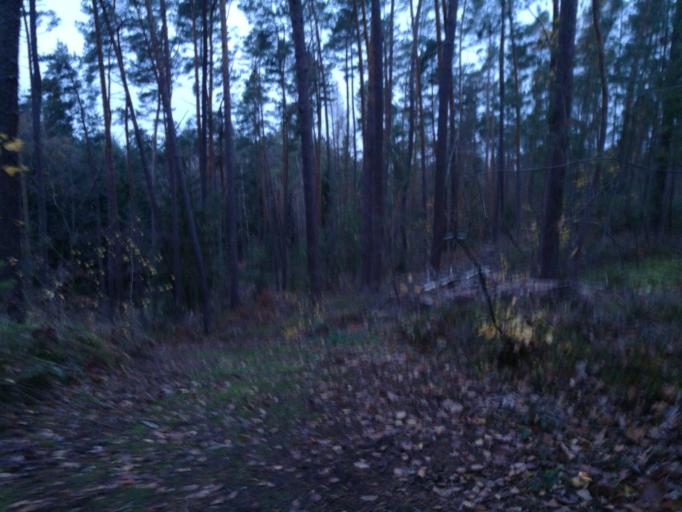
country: DE
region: Bavaria
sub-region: Regierungsbezirk Mittelfranken
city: Seukendorf
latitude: 49.4708
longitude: 10.8824
